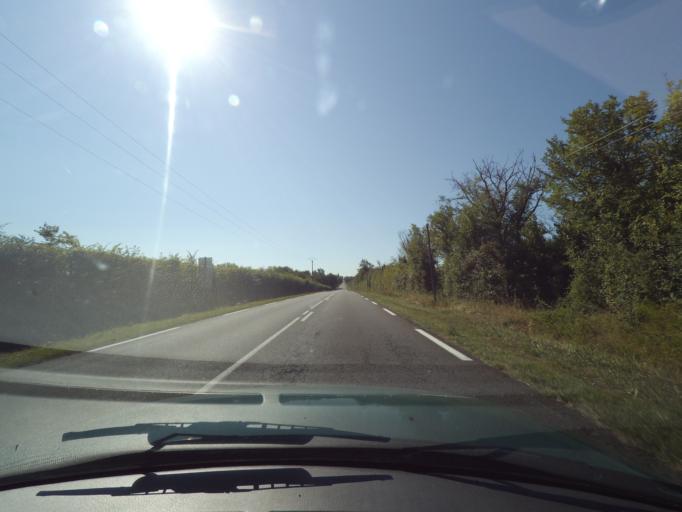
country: FR
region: Poitou-Charentes
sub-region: Departement de la Vienne
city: Lussac-les-Chateaux
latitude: 46.3689
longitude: 0.7656
